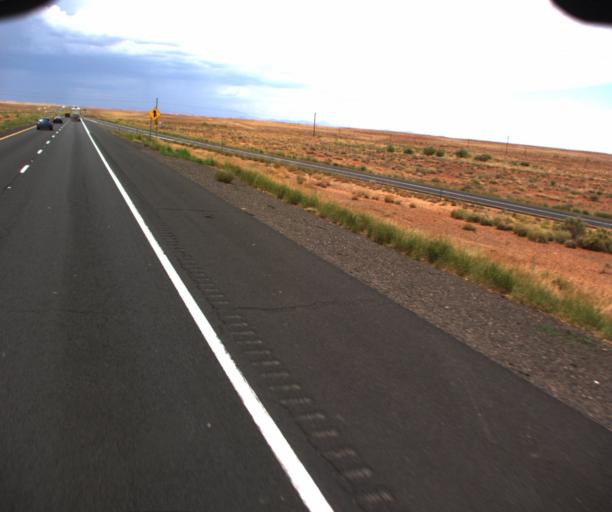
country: US
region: Arizona
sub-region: Coconino County
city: LeChee
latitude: 35.0947
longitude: -110.9324
